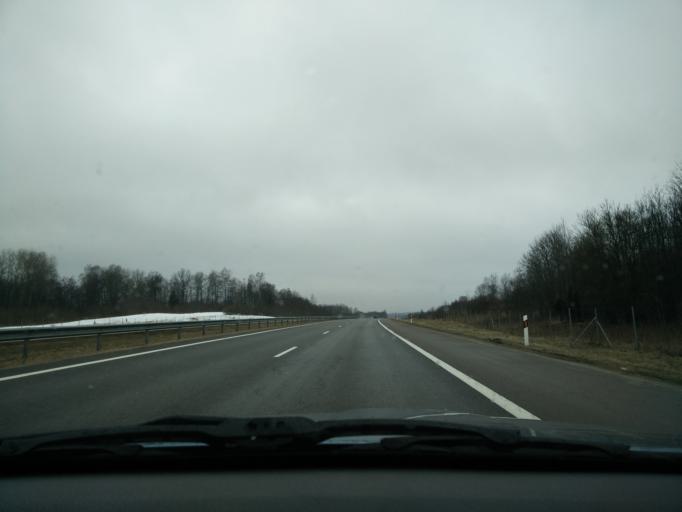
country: LT
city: Silale
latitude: 55.5413
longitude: 22.2887
